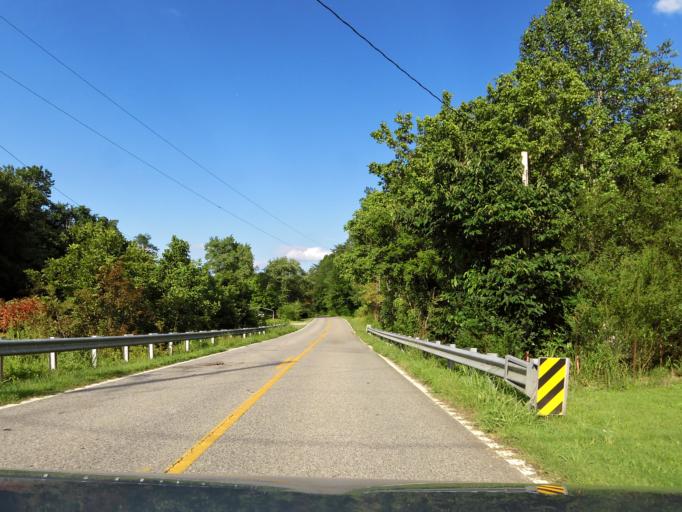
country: US
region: Tennessee
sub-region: Loudon County
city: Greenback
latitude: 35.6196
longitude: -84.0363
